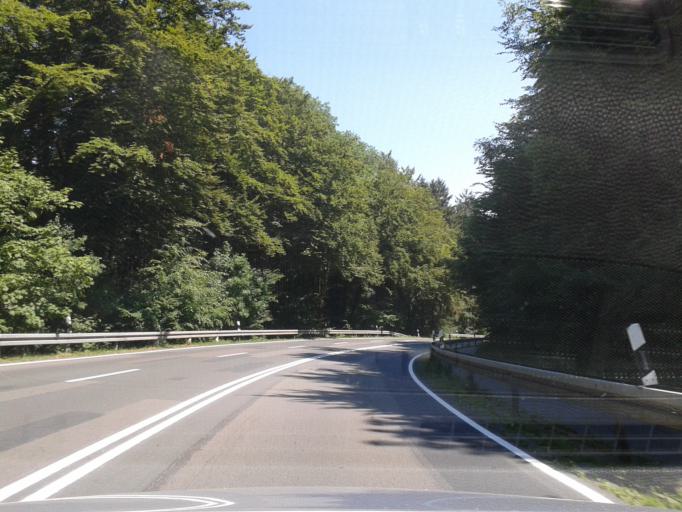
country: DE
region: Lower Saxony
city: Bad Pyrmont
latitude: 51.9812
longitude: 9.2089
